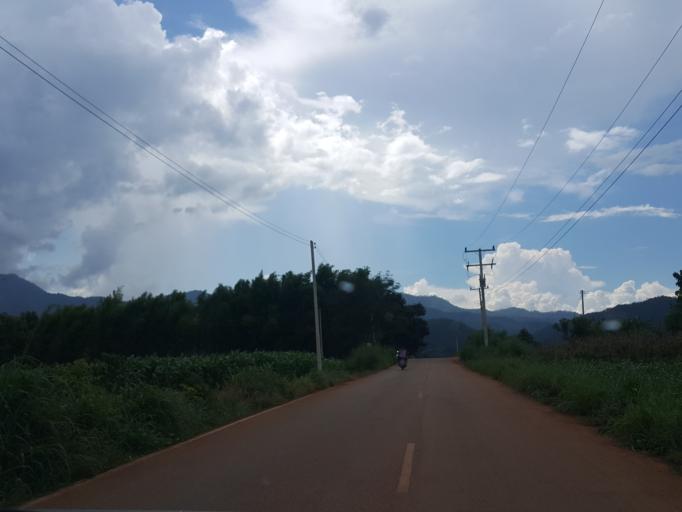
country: TH
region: Chiang Mai
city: Phrao
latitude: 19.3342
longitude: 99.1657
